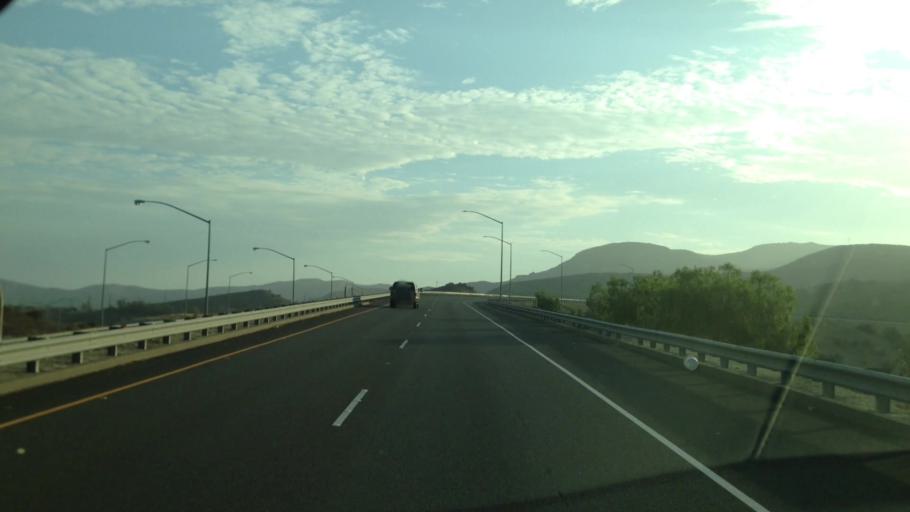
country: US
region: California
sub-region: Orange County
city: Foothill Ranch
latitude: 33.7080
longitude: -117.7247
